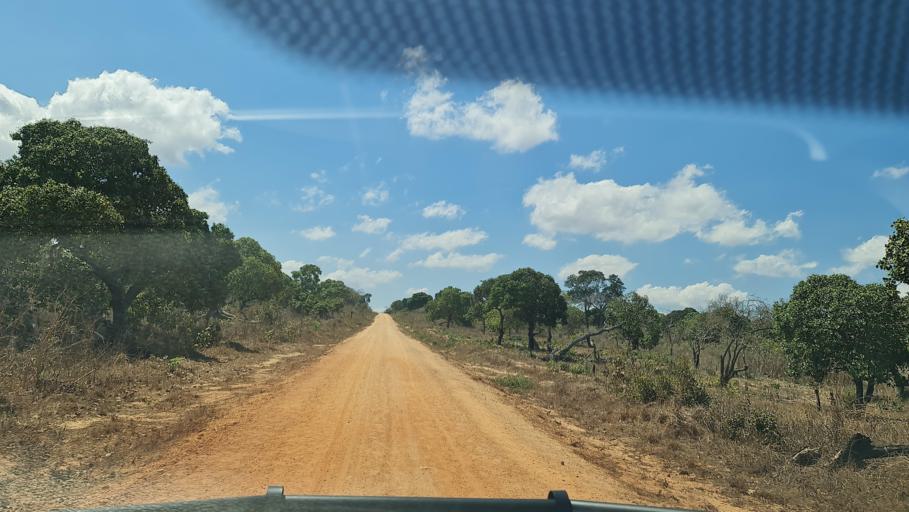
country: MZ
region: Nampula
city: Nacala
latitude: -14.1736
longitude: 40.2038
